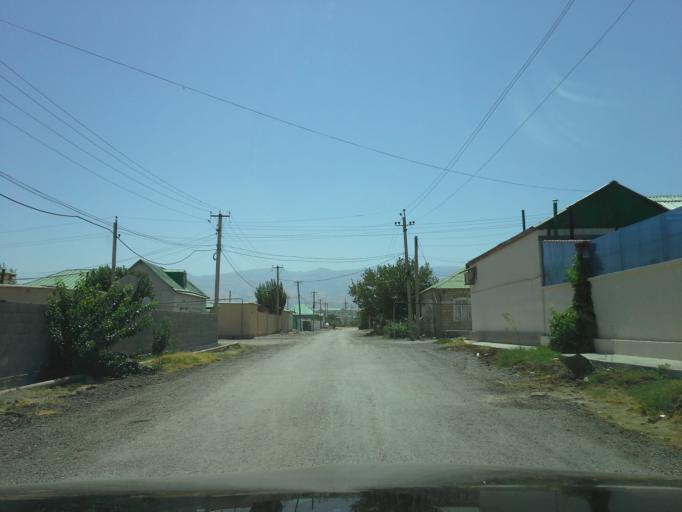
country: TM
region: Ahal
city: Ashgabat
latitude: 37.9973
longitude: 58.3223
